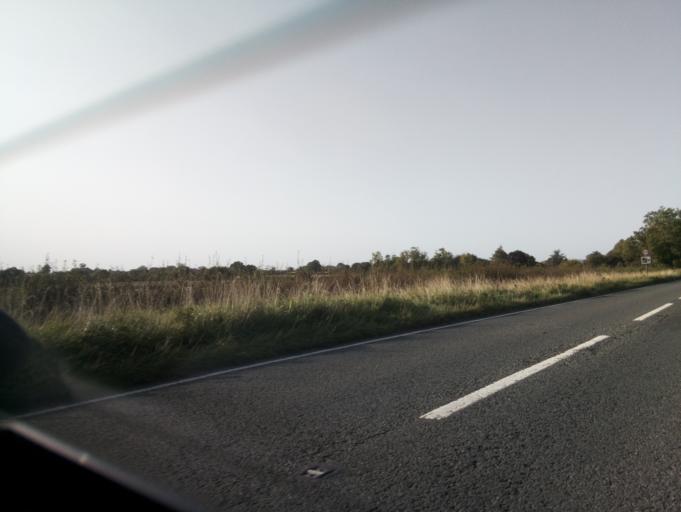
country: GB
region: England
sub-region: Gloucestershire
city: Gloucester
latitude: 51.9386
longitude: -2.2960
